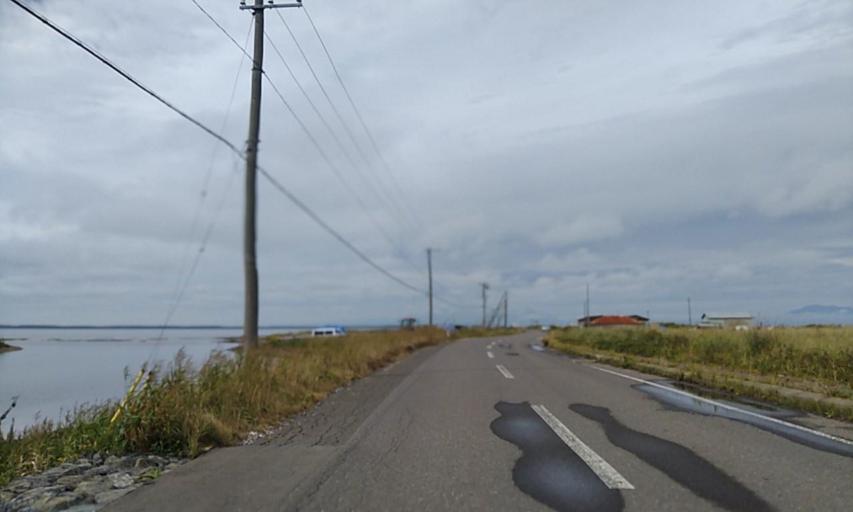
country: JP
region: Hokkaido
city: Shibetsu
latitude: 43.6096
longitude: 145.2719
